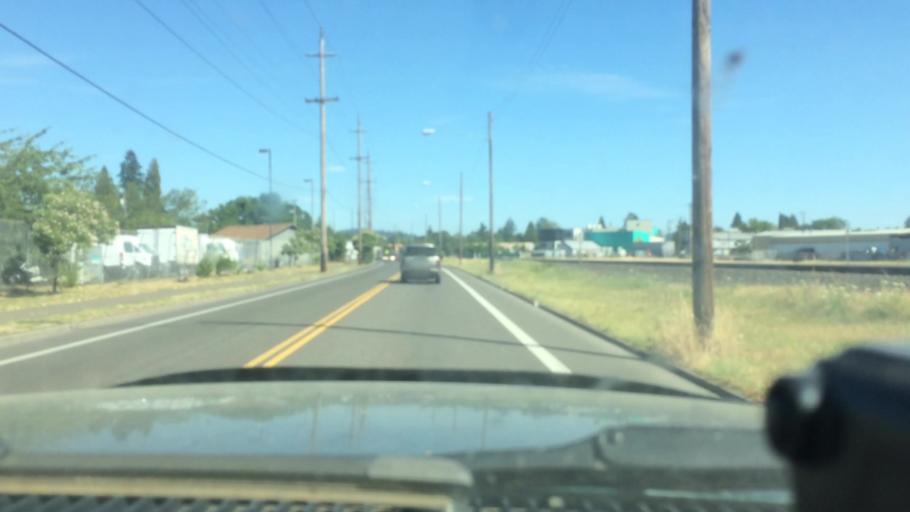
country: US
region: Oregon
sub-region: Lane County
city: Eugene
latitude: 44.0607
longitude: -123.1140
